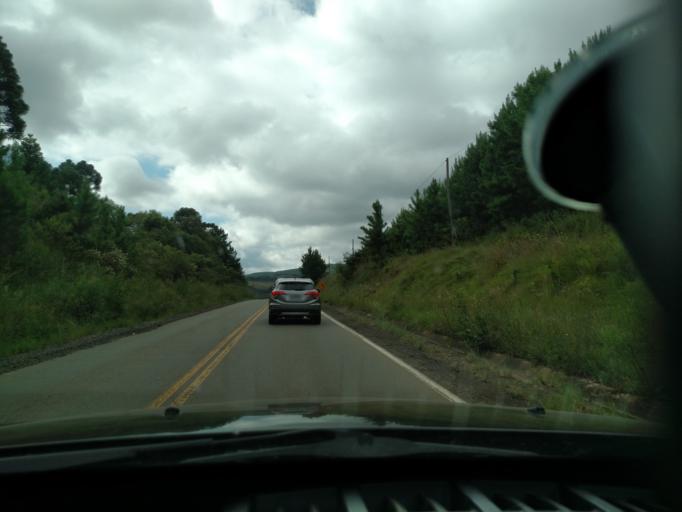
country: BR
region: Santa Catarina
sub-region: Lages
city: Lages
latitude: -27.8629
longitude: -50.2110
